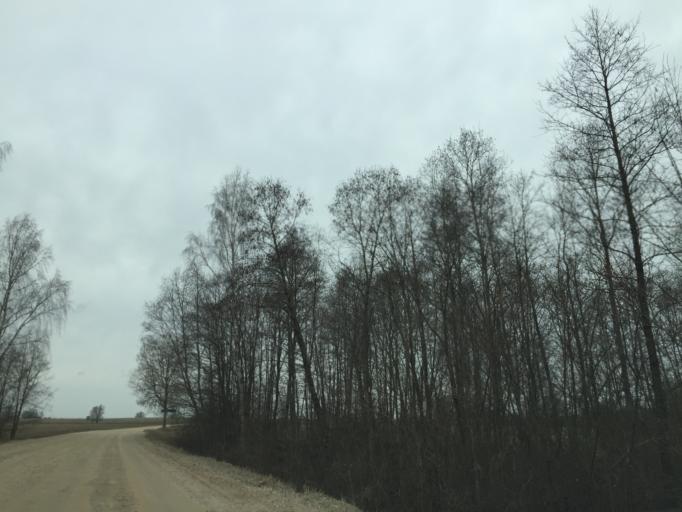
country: LV
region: Livani
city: Livani
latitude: 56.2789
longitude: 26.1837
